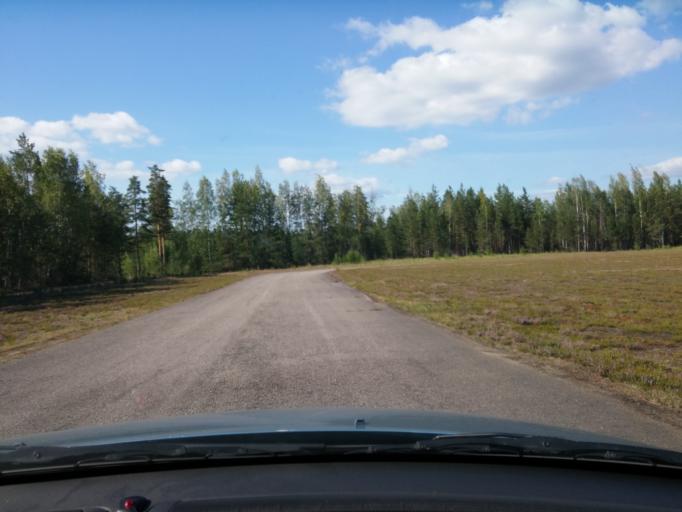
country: FI
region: Uusimaa
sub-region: Helsinki
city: Kaerkoelae
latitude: 60.7413
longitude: 24.0919
